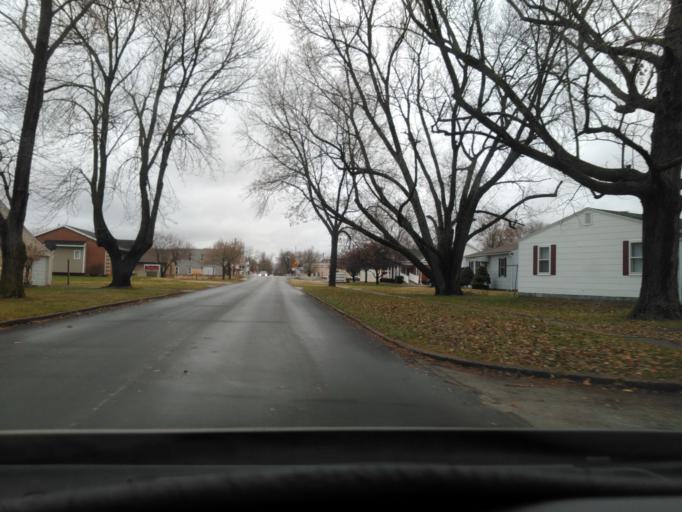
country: US
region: Illinois
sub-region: Effingham County
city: Altamont
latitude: 39.0632
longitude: -88.7479
